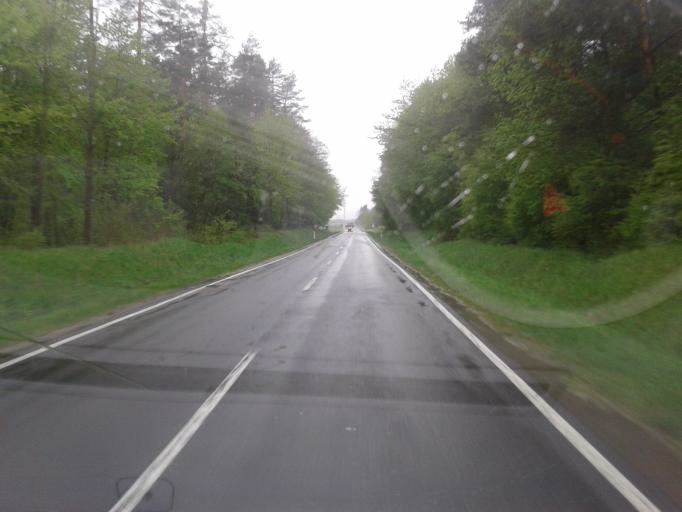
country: PL
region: Subcarpathian Voivodeship
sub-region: Powiat lubaczowski
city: Narol
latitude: 50.3177
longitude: 23.2565
